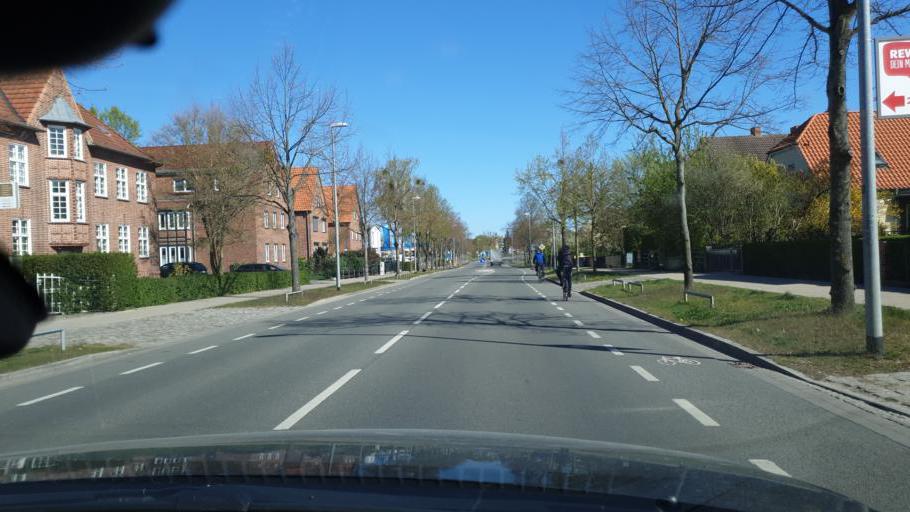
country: DE
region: Mecklenburg-Vorpommern
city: Werdervorstadt
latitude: 53.6415
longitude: 11.4247
